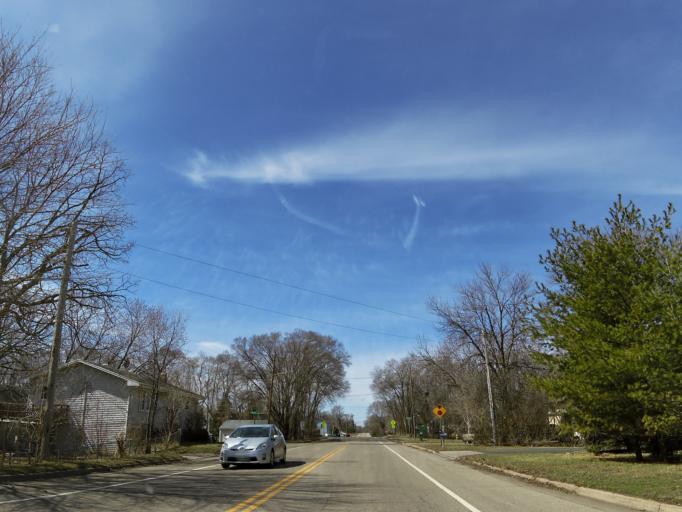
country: US
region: Minnesota
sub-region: Ramsey County
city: North Saint Paul
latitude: 44.9921
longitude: -93.0435
